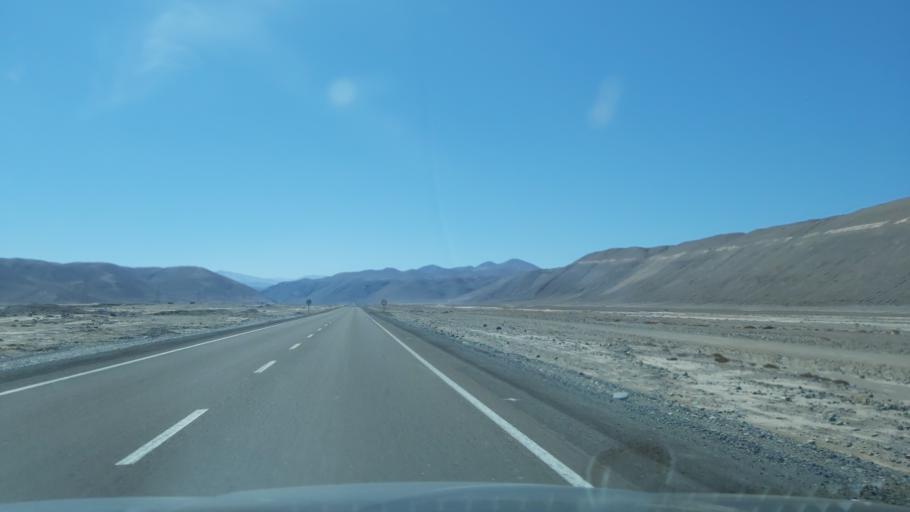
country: CL
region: Atacama
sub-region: Provincia de Chanaral
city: Diego de Almagro
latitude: -26.3522
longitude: -69.8954
